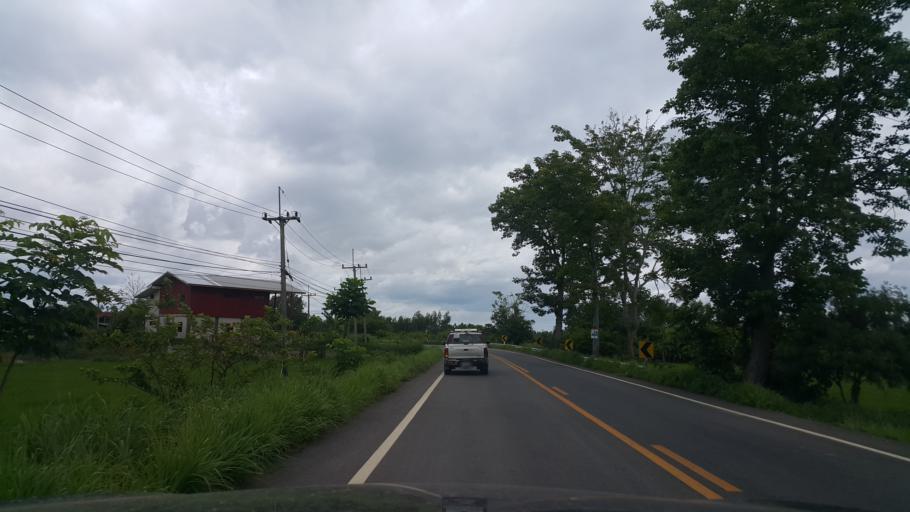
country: TH
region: Sukhothai
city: Sukhothai
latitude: 16.9185
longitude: 99.8558
